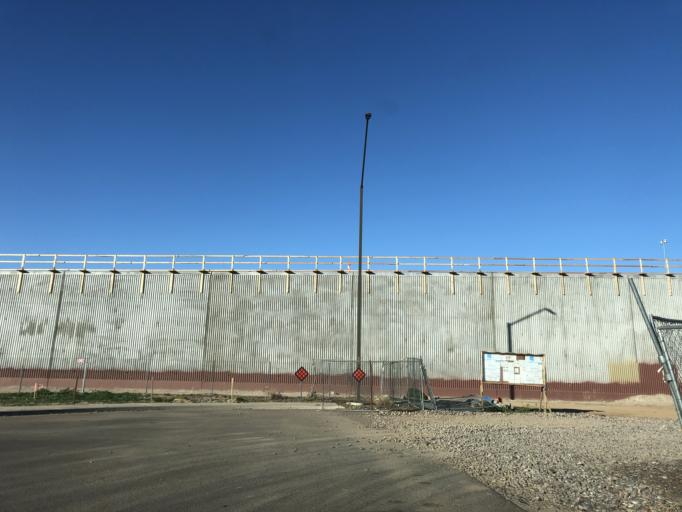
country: US
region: Arizona
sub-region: Maricopa County
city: Avondale
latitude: 33.4569
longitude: -112.3239
